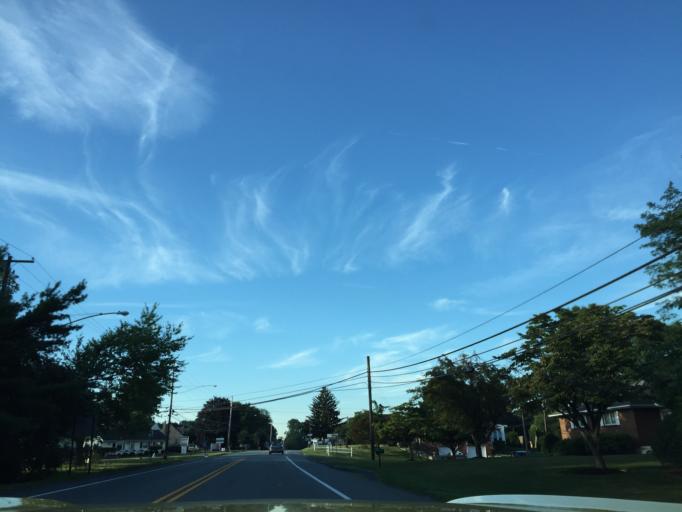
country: US
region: Pennsylvania
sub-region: Lehigh County
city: Dorneyville
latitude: 40.5758
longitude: -75.5202
